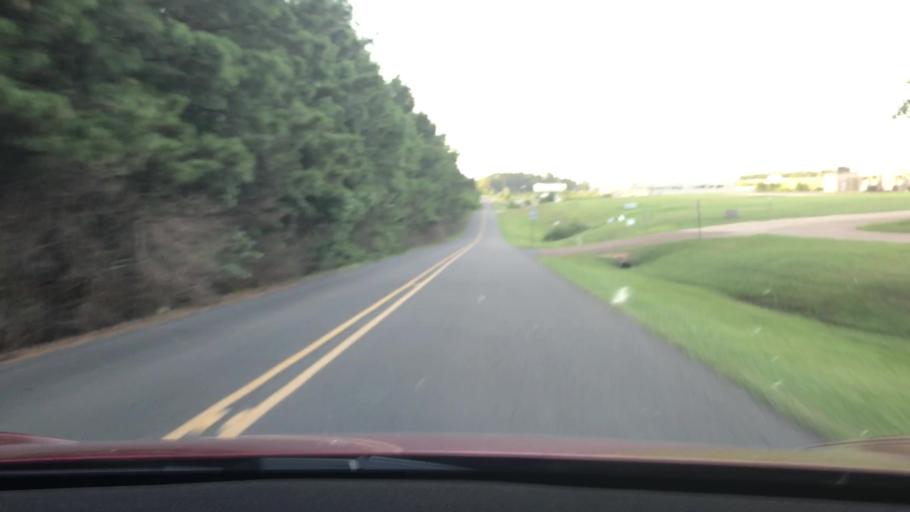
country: US
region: Louisiana
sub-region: Bossier Parish
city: Bossier City
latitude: 32.3916
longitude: -93.7548
